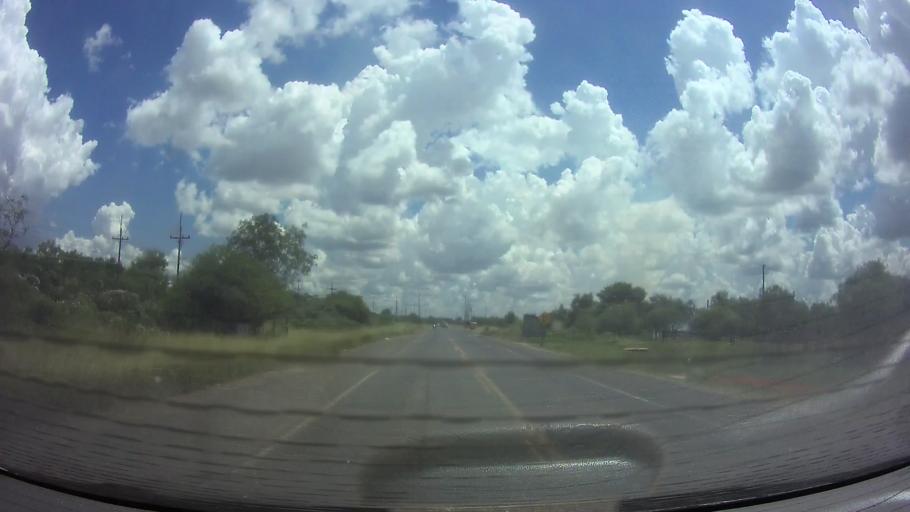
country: PY
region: Central
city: Colonia Mariano Roque Alonso
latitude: -25.1746
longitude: -57.5745
